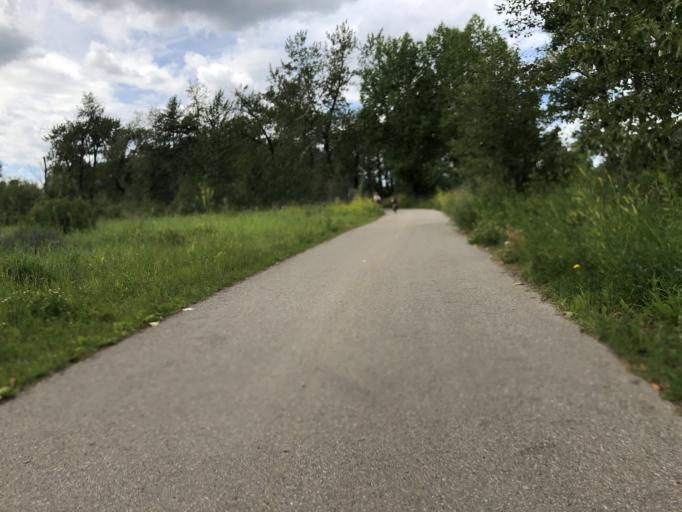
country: CA
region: Alberta
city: Calgary
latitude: 51.0016
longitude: -114.0221
